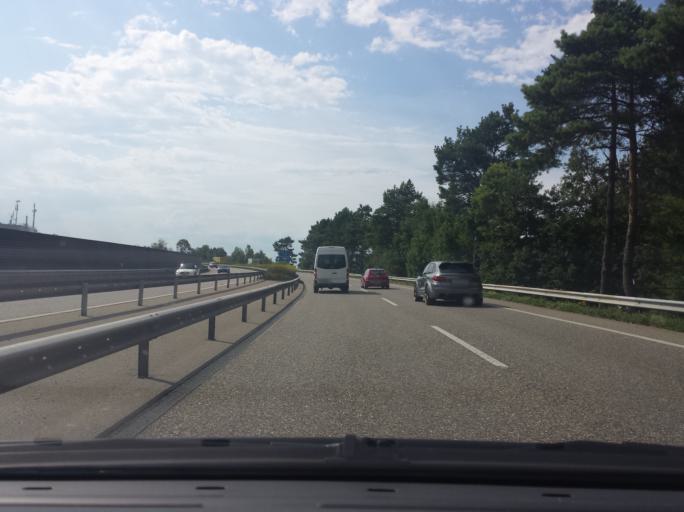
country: CH
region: Saint Gallen
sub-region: Wahlkreis Rheintal
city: Rheineck
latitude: 47.4794
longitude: 9.5824
